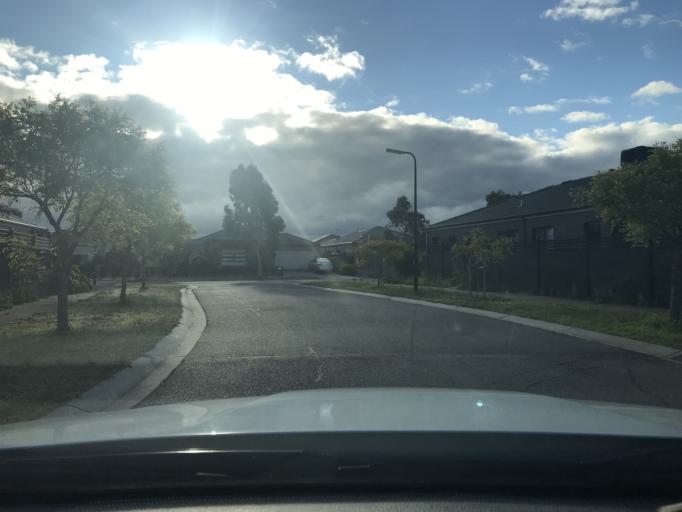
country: AU
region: Victoria
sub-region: Hume
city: Craigieburn
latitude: -37.5794
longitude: 144.9058
